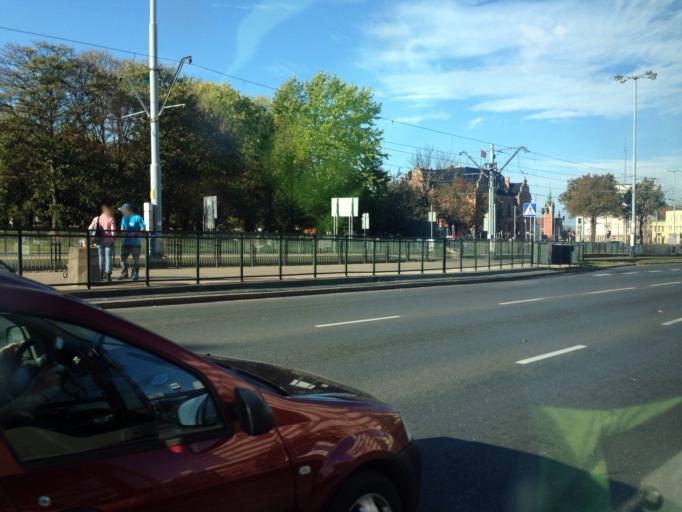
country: PL
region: Pomeranian Voivodeship
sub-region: Gdansk
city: Gdansk
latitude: 54.3506
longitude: 18.6464
